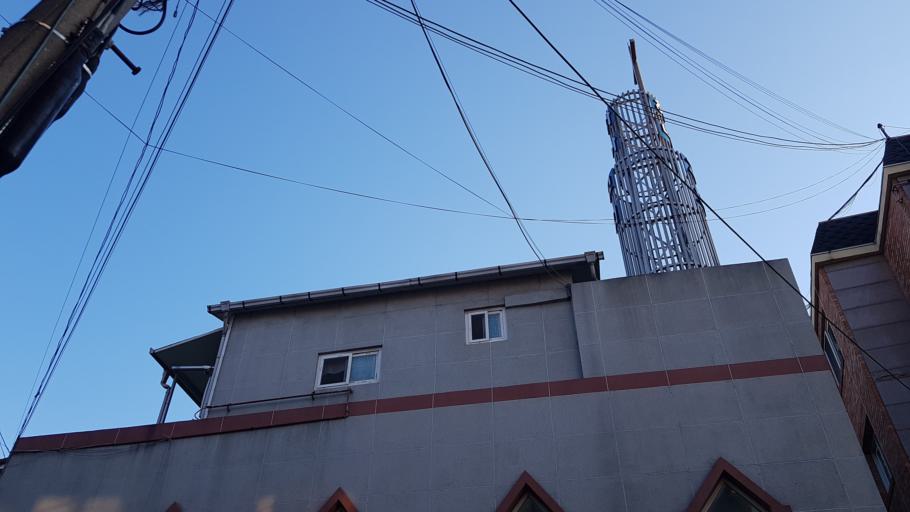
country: KR
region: Gyeonggi-do
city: Kwangmyong
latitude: 37.4976
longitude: 126.9365
